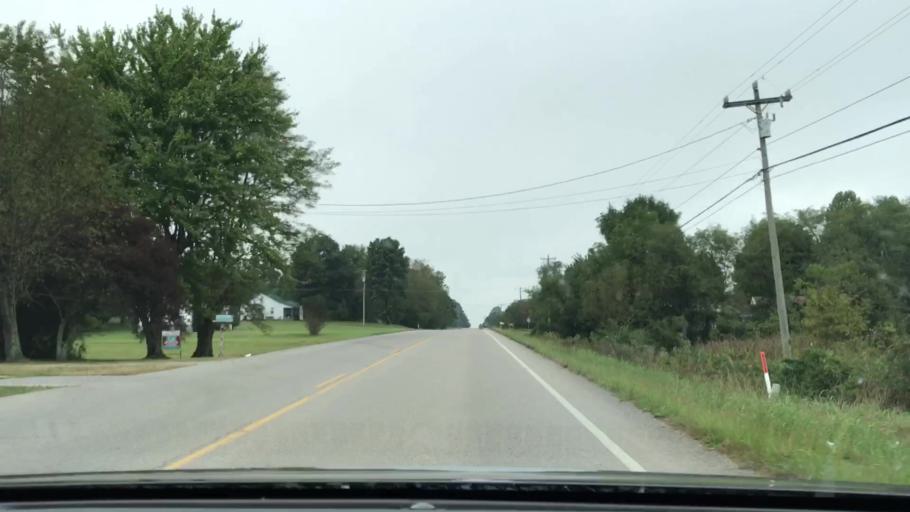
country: US
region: Tennessee
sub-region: Sumner County
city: Portland
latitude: 36.5081
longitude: -86.4993
